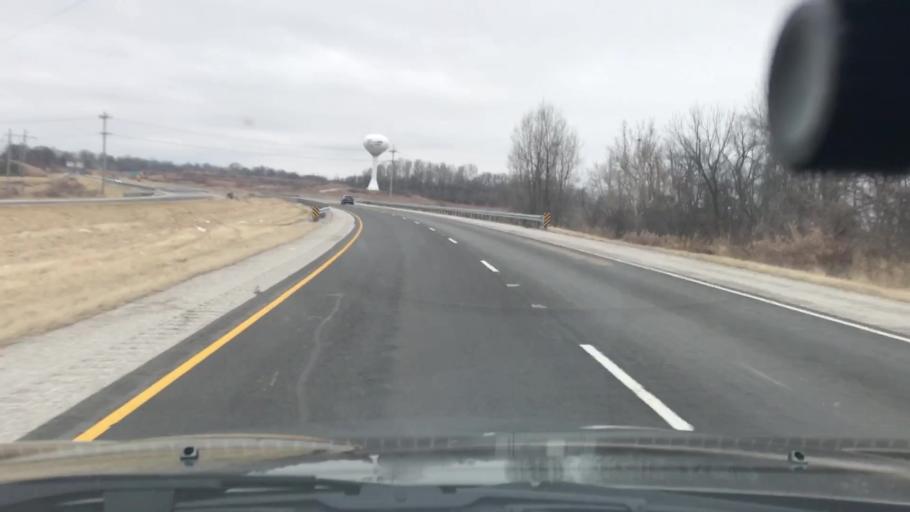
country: US
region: Illinois
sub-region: Madison County
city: Rosewood Heights
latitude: 38.8726
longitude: -90.0610
